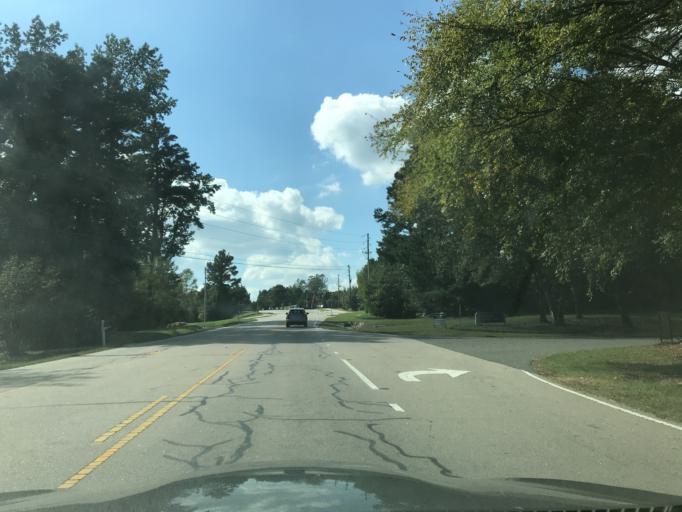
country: US
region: North Carolina
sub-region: Wake County
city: Rolesville
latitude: 35.8713
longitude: -78.5549
